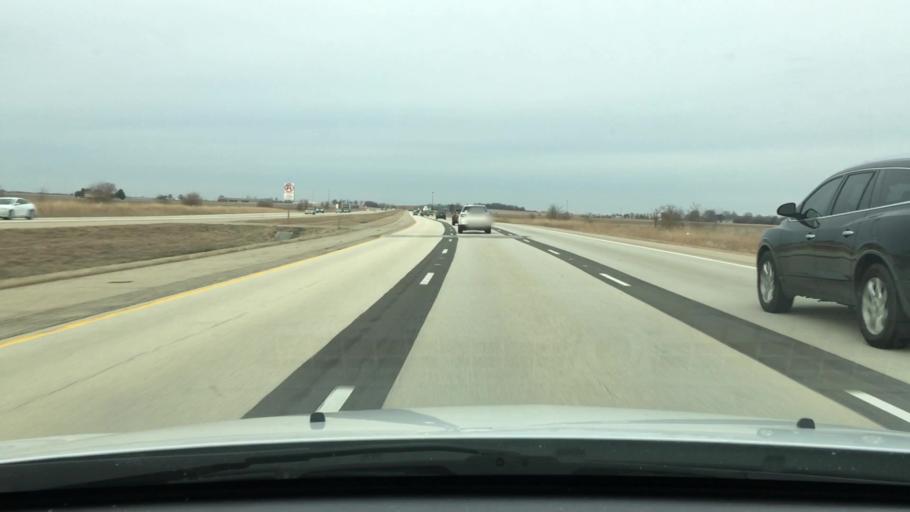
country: US
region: Illinois
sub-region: Sangamon County
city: Williamsville
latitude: 40.0062
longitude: -89.5009
